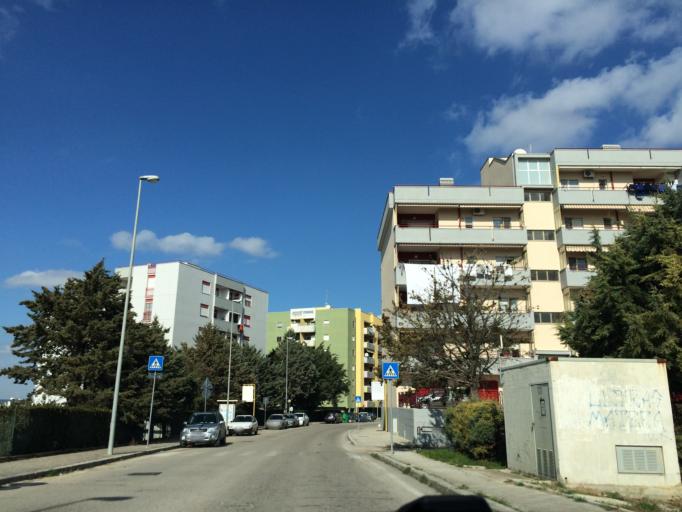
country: IT
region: Basilicate
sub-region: Provincia di Matera
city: Matera
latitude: 40.6696
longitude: 16.5864
